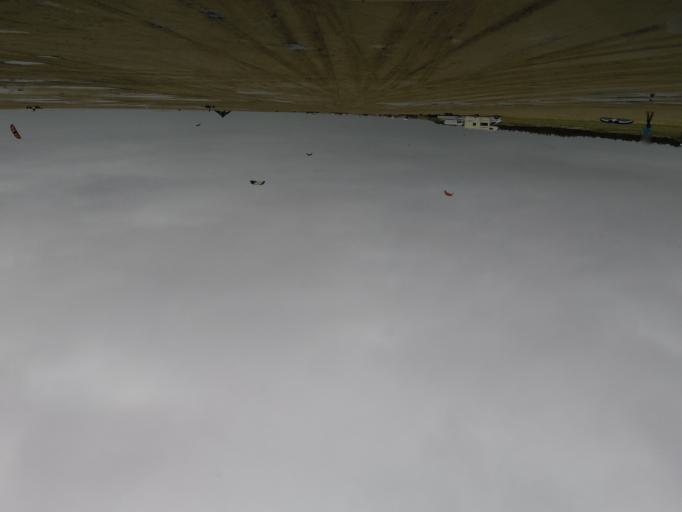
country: DE
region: Schleswig-Holstein
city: List
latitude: 55.0861
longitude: 8.5087
